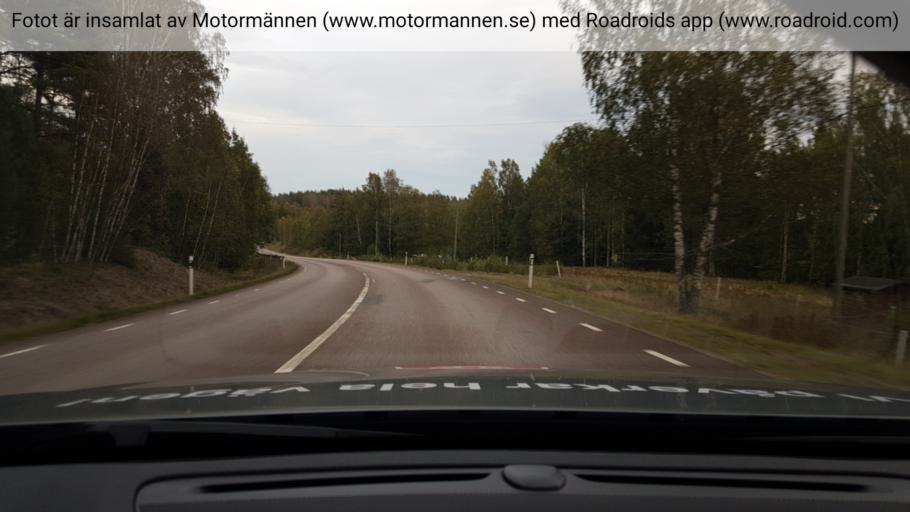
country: SE
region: Vaestra Goetaland
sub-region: Amals Kommun
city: Amal
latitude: 59.0724
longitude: 12.6370
